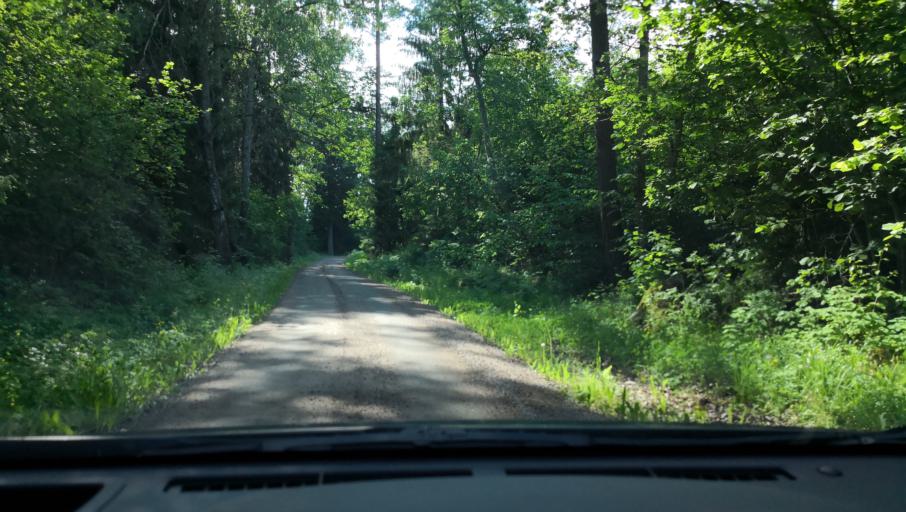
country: SE
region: Uppsala
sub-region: Enkopings Kommun
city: Orsundsbro
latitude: 59.8357
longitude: 17.2283
